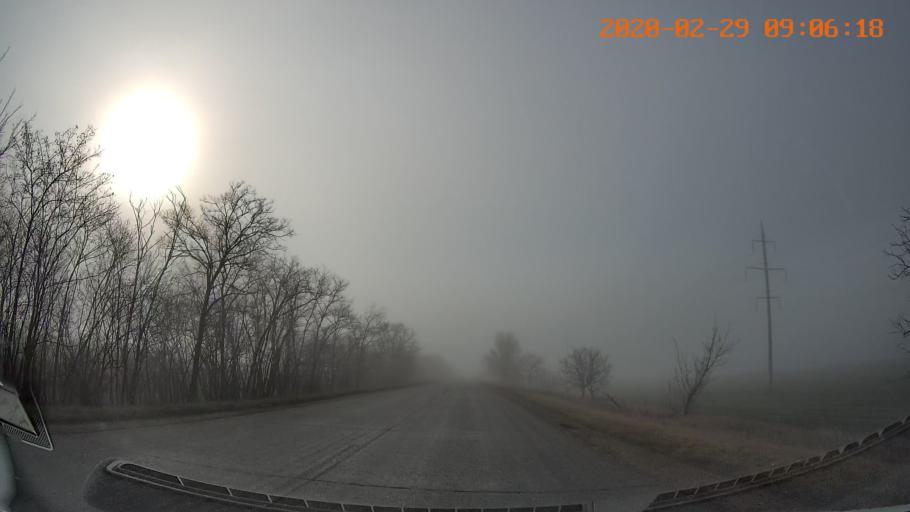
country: MD
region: Telenesti
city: Tiraspolul Nou
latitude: 46.8775
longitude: 29.7440
